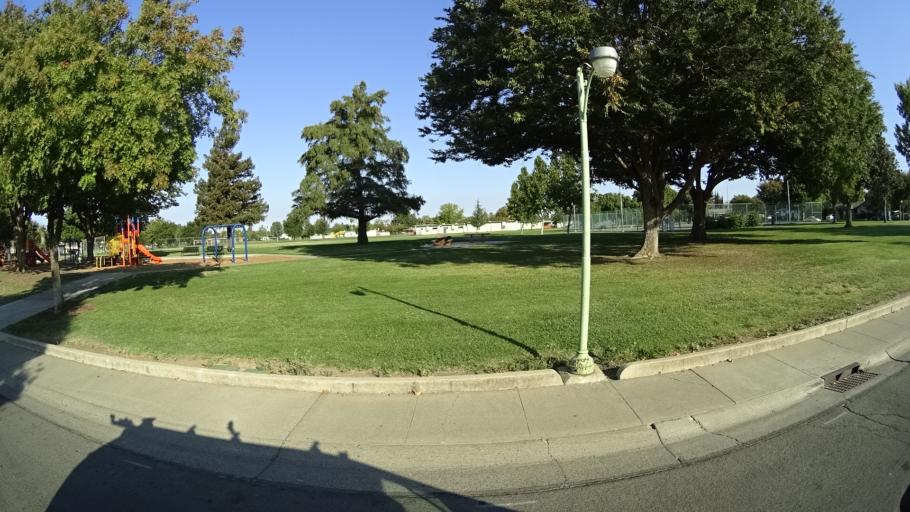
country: US
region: California
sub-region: Sacramento County
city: Parkway
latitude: 38.4903
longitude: -121.4958
